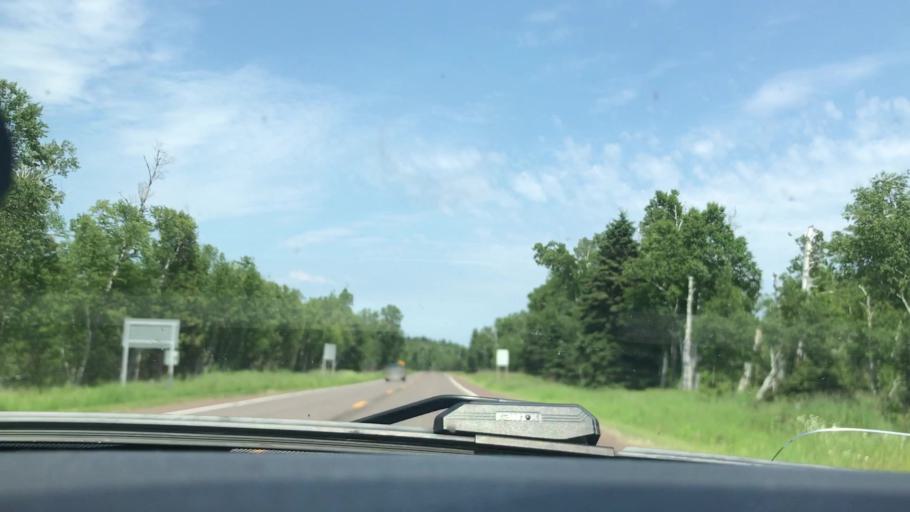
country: US
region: Minnesota
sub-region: Lake County
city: Silver Bay
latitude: 47.4900
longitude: -90.9834
